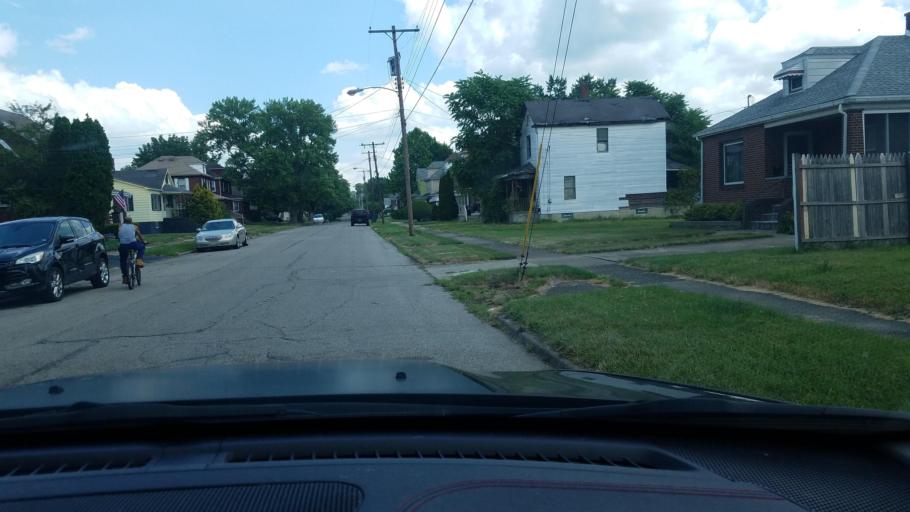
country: US
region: Ohio
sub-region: Mahoning County
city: Campbell
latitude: 41.0775
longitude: -80.5934
